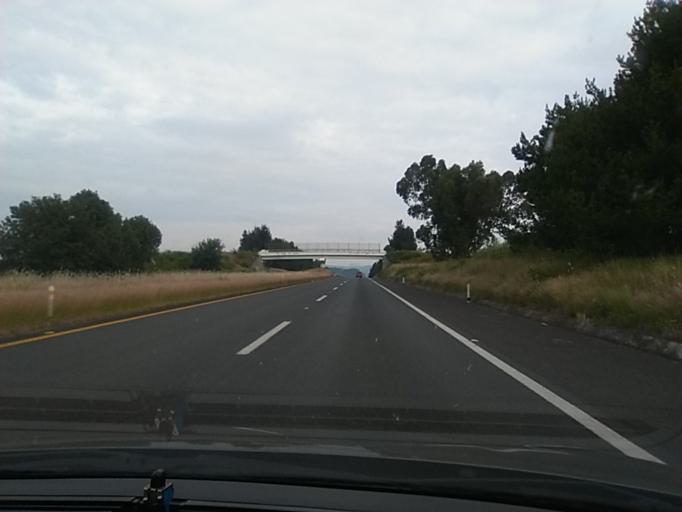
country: MX
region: Michoacan
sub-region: Puruandiro
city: San Lorenzo
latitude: 19.9586
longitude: -101.6662
